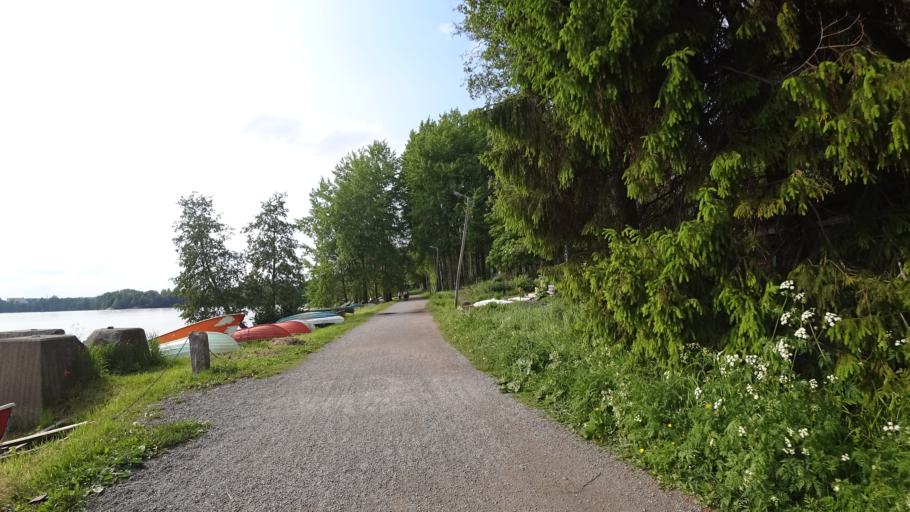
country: FI
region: Pirkanmaa
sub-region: Tampere
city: Tampere
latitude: 61.5015
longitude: 23.7062
